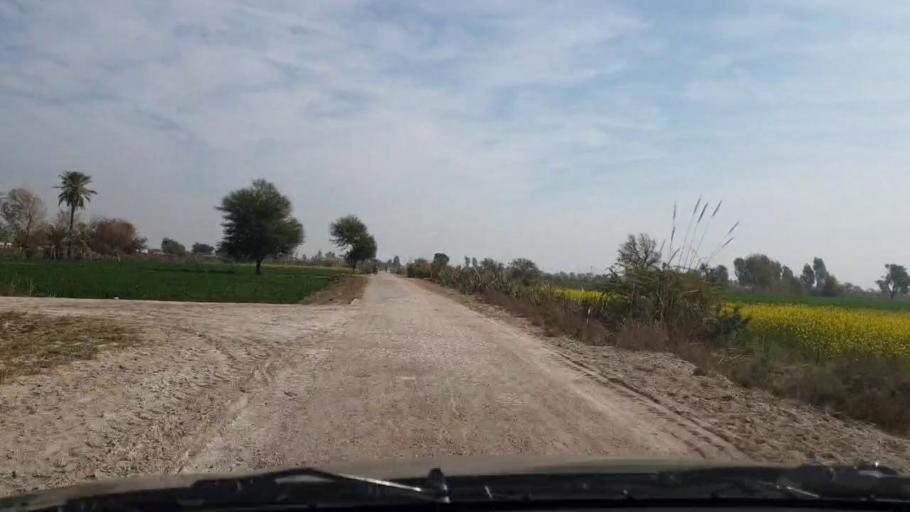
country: PK
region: Sindh
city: Jam Sahib
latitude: 26.2693
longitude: 68.7104
